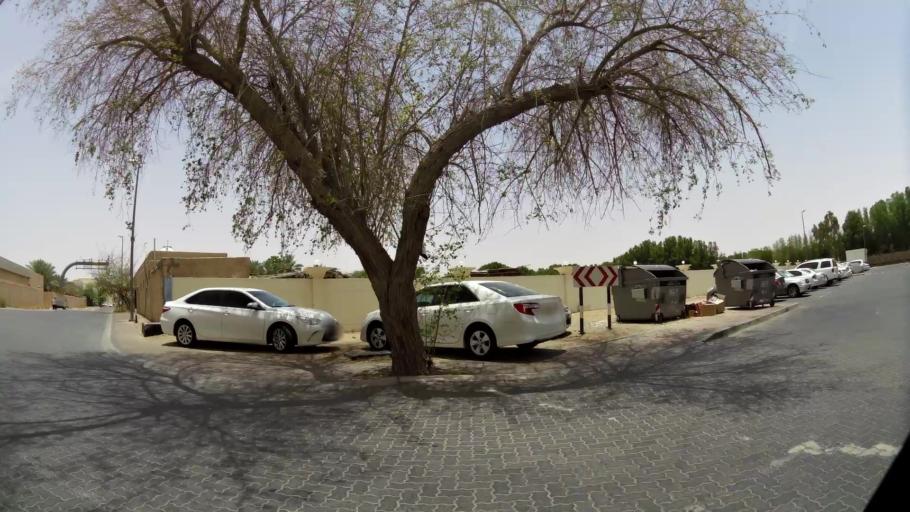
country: AE
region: Abu Dhabi
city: Al Ain
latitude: 24.2233
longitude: 55.7276
